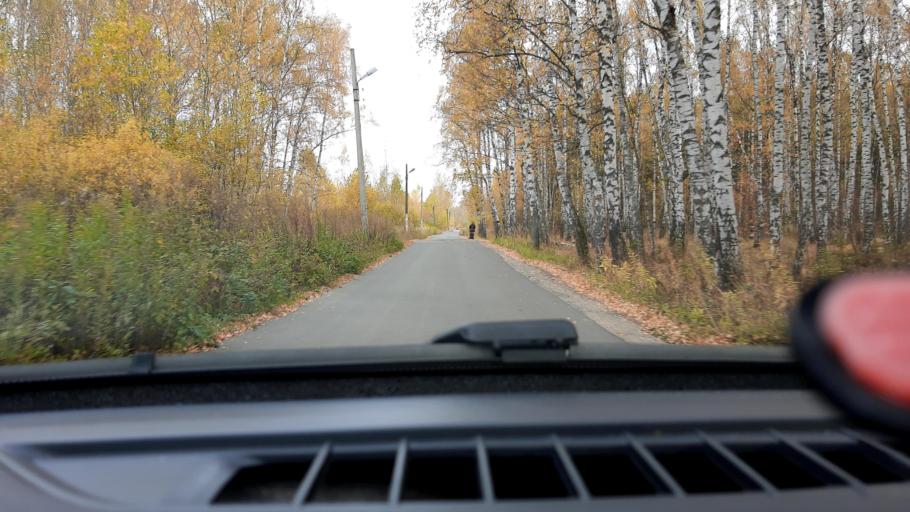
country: RU
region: Nizjnij Novgorod
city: Gorbatovka
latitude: 56.2892
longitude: 43.8309
